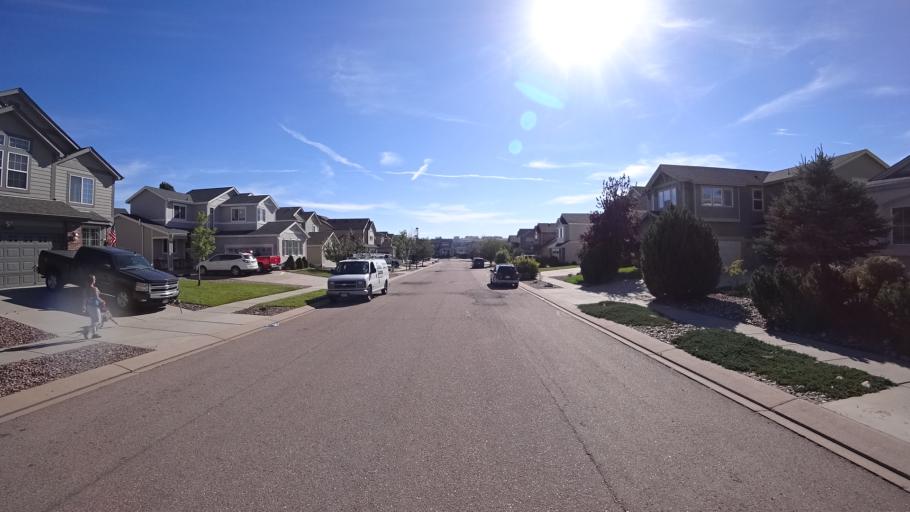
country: US
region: Colorado
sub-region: El Paso County
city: Black Forest
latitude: 38.9436
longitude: -104.7358
